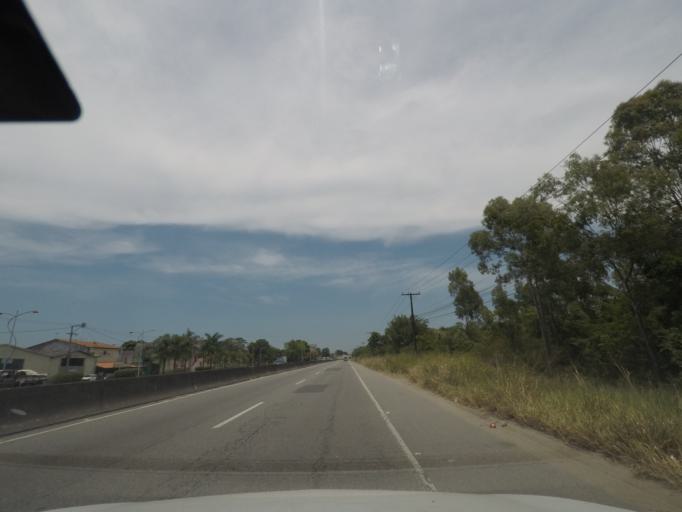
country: BR
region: Rio de Janeiro
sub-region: Marica
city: Marica
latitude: -22.9170
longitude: -42.8510
